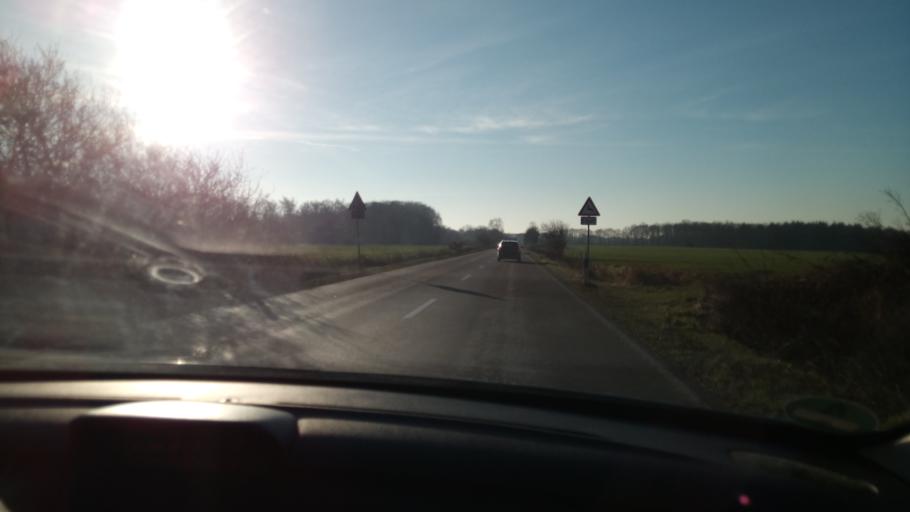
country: DE
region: Schleswig-Holstein
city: Basedow
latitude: 53.4119
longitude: 10.5681
